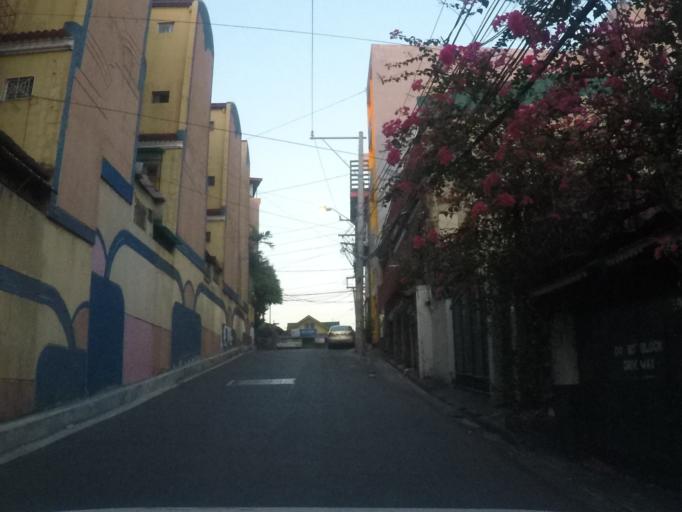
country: PH
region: Metro Manila
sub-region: San Juan
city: San Juan
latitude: 14.6067
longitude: 121.0271
